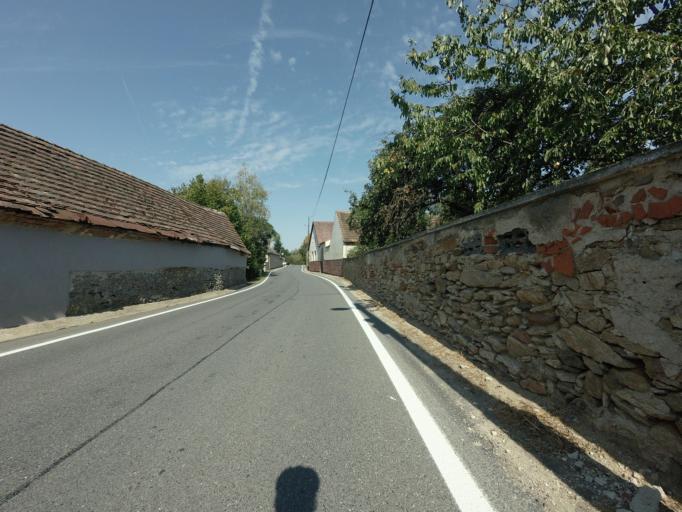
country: CZ
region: Jihocesky
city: Bernartice
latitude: 49.3822
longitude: 14.3651
